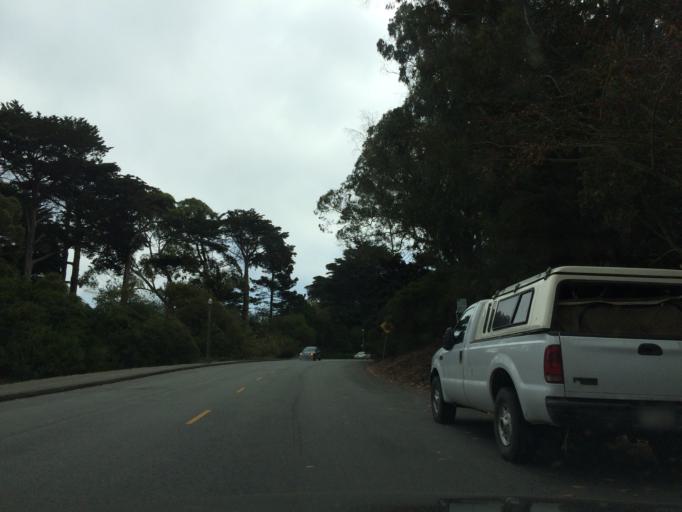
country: US
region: California
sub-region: San Francisco County
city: San Francisco
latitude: 37.7667
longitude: -122.4634
